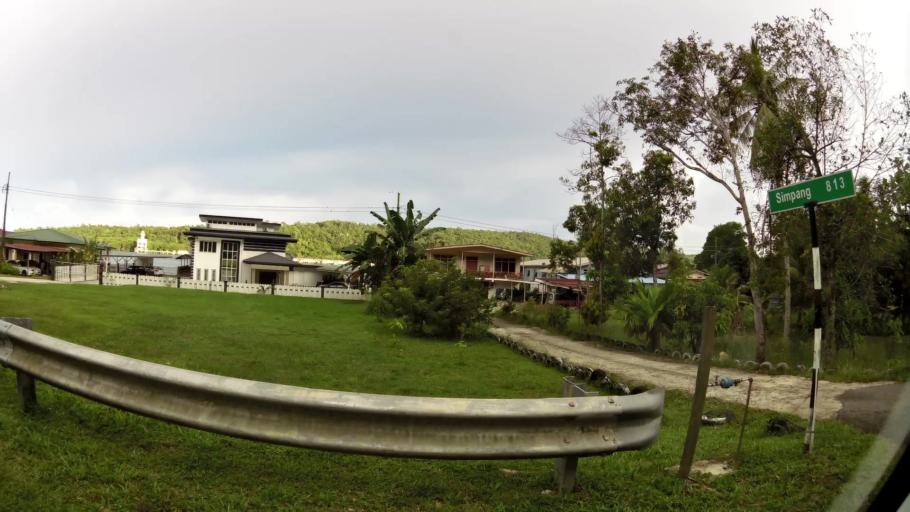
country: BN
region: Brunei and Muara
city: Bandar Seri Begawan
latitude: 4.9221
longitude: 115.0100
